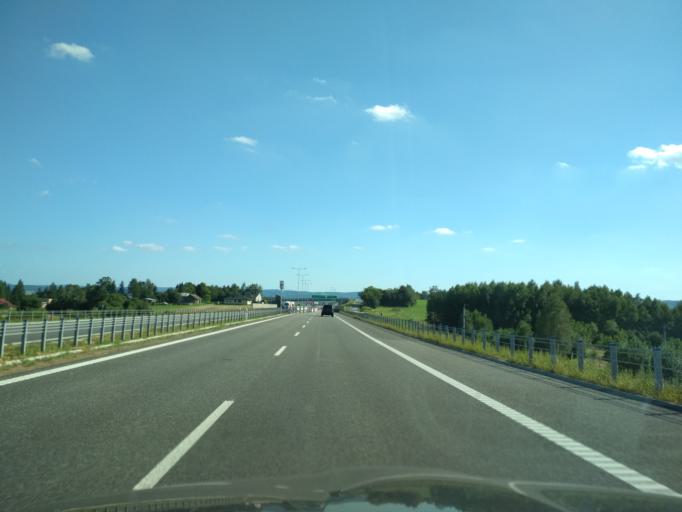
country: PL
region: Subcarpathian Voivodeship
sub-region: Powiat rzeszowski
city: Kielanowka
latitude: 50.0220
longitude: 21.9218
